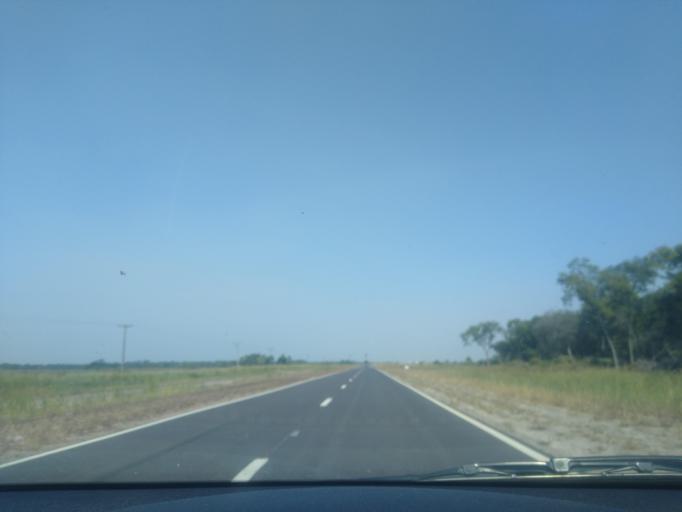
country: AR
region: Chaco
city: Fontana
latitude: -27.5759
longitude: -59.1790
